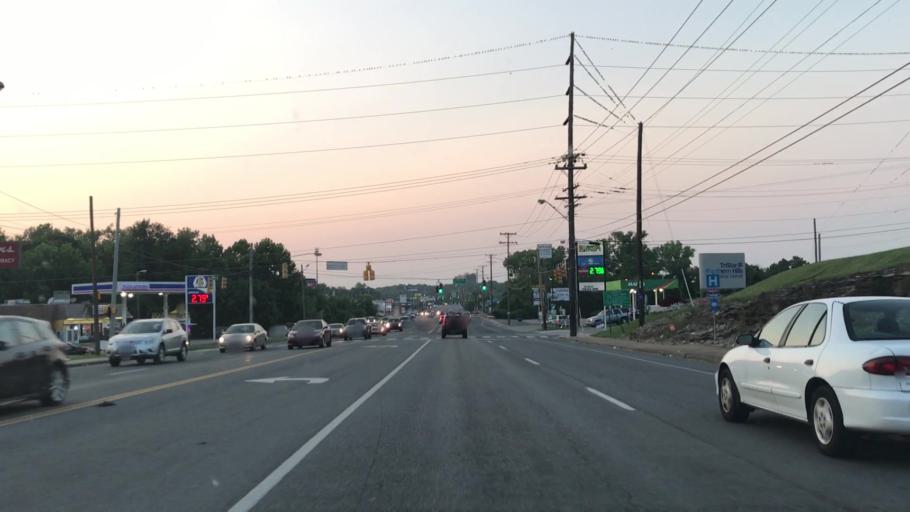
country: US
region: Tennessee
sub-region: Davidson County
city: Oak Hill
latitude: 36.0765
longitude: -86.7253
